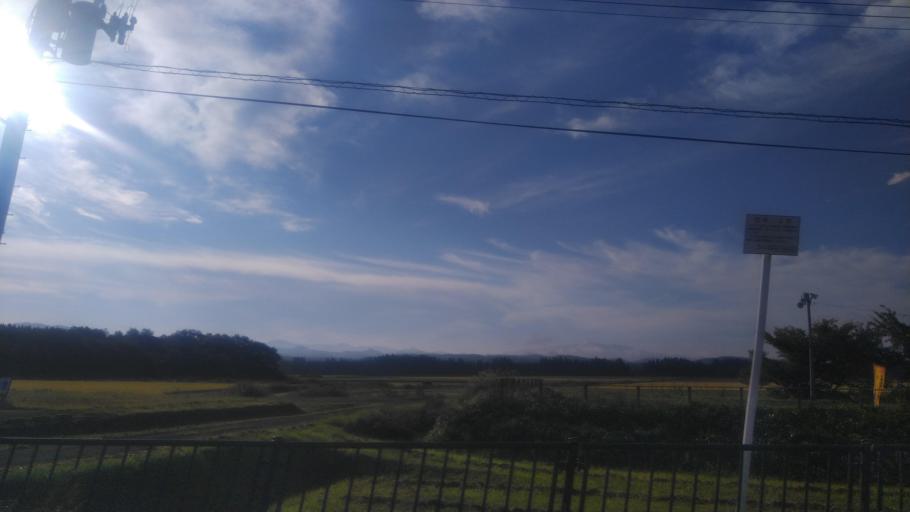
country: JP
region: Akita
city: Takanosu
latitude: 40.2533
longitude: 140.3848
